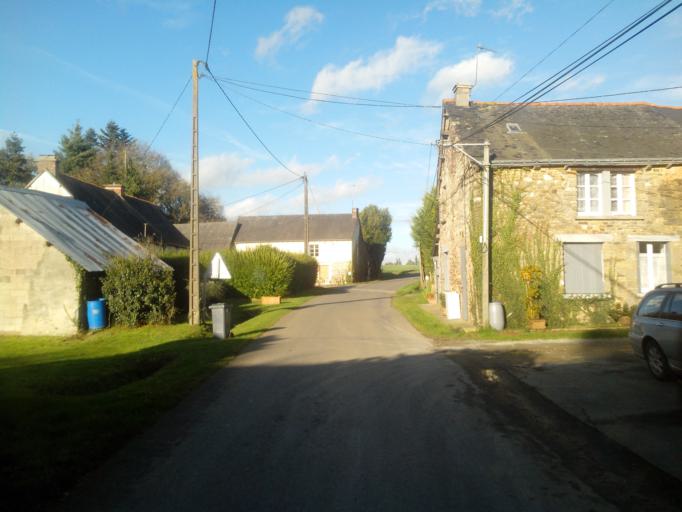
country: FR
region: Brittany
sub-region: Departement du Morbihan
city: Guilliers
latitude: 48.0848
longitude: -2.4139
